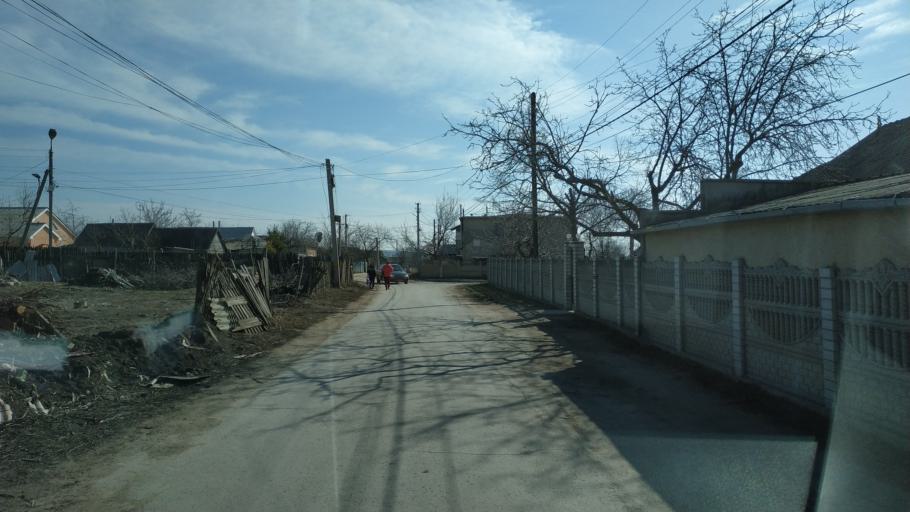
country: MD
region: Nisporeni
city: Nisporeni
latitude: 47.0800
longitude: 28.1616
